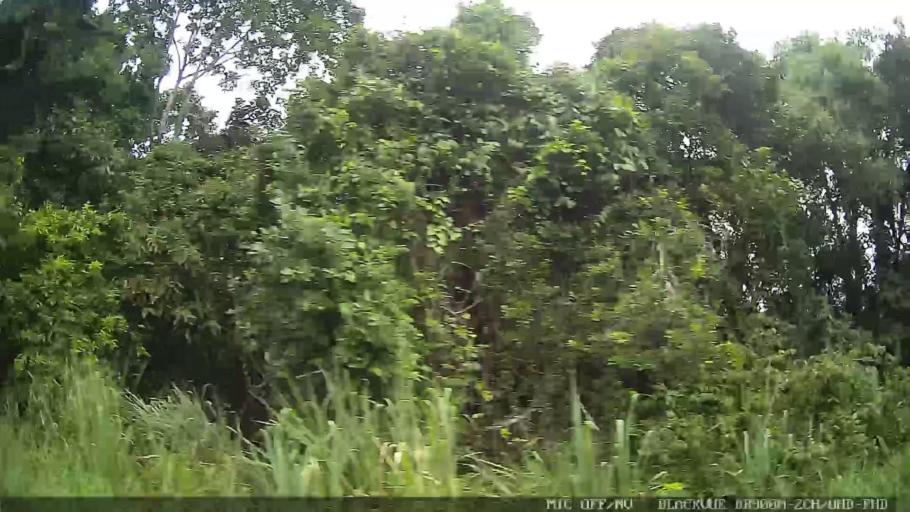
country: BR
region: Sao Paulo
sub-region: Iguape
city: Iguape
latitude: -24.6625
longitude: -47.4210
